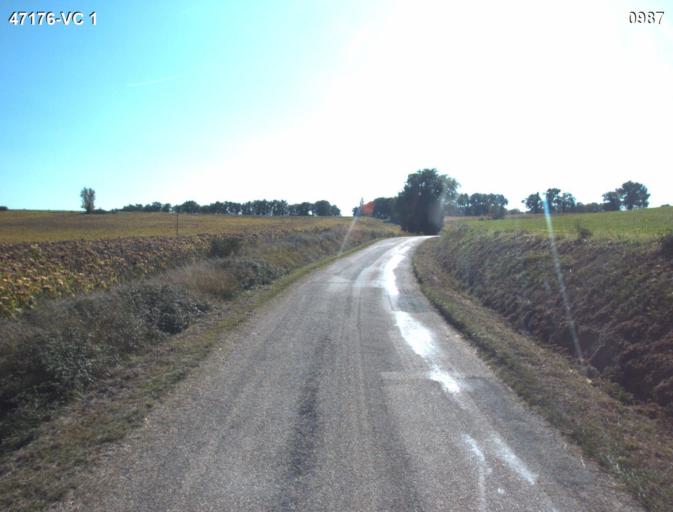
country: FR
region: Aquitaine
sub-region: Departement du Lot-et-Garonne
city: Lavardac
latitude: 44.2016
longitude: 0.2927
